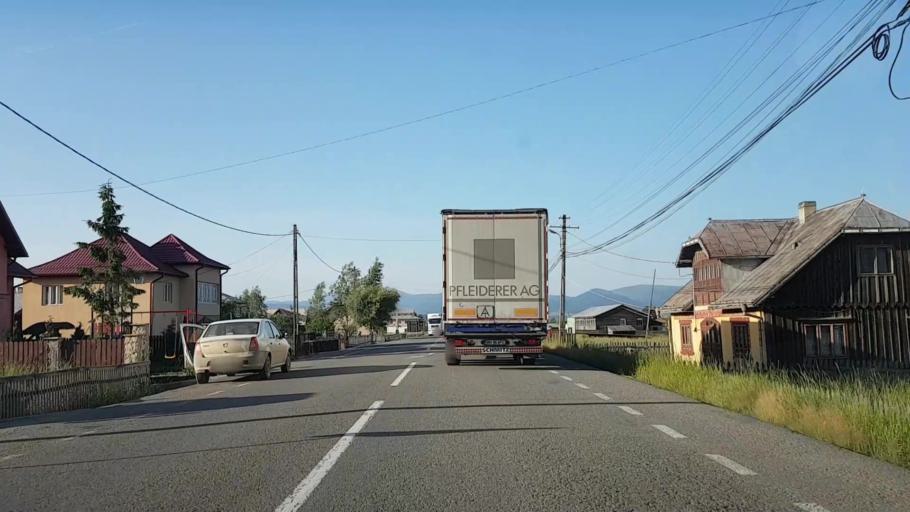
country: RO
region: Suceava
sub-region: Comuna Poiana Stampei
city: Poiana Stampei
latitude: 47.3103
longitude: 25.1279
